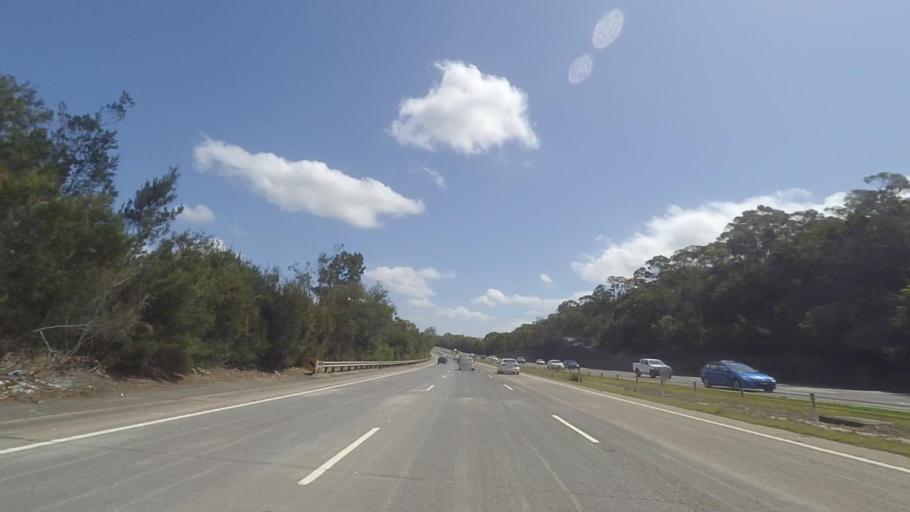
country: AU
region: New South Wales
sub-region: Hornsby Shire
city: Mount Colah
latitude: -33.6669
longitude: 151.1226
